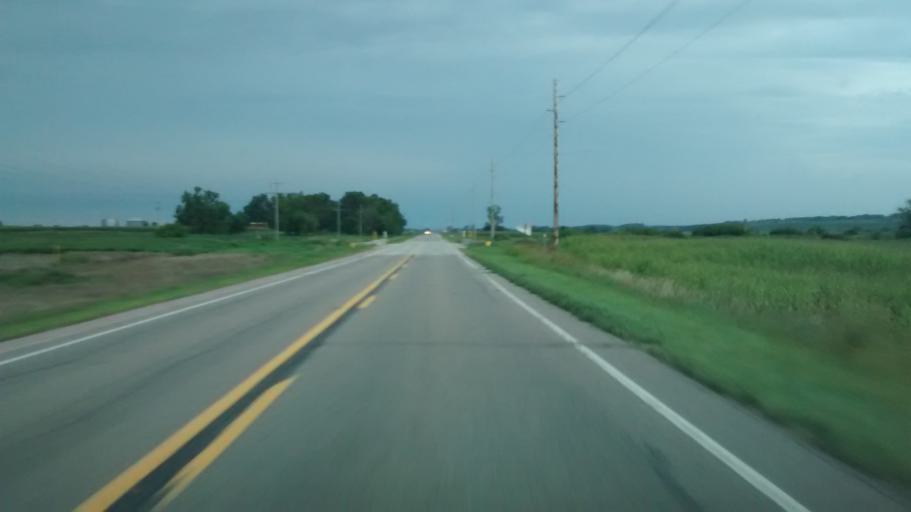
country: US
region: Iowa
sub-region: Woodbury County
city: Moville
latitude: 42.5359
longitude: -96.0329
